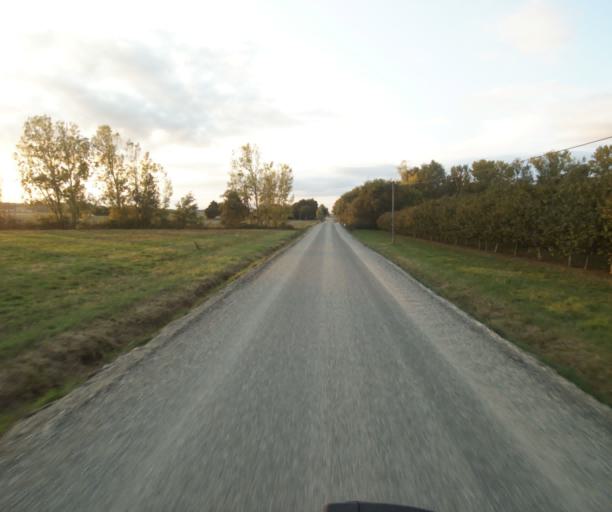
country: FR
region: Midi-Pyrenees
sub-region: Departement du Tarn-et-Garonne
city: Verdun-sur-Garonne
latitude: 43.8327
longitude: 1.2237
